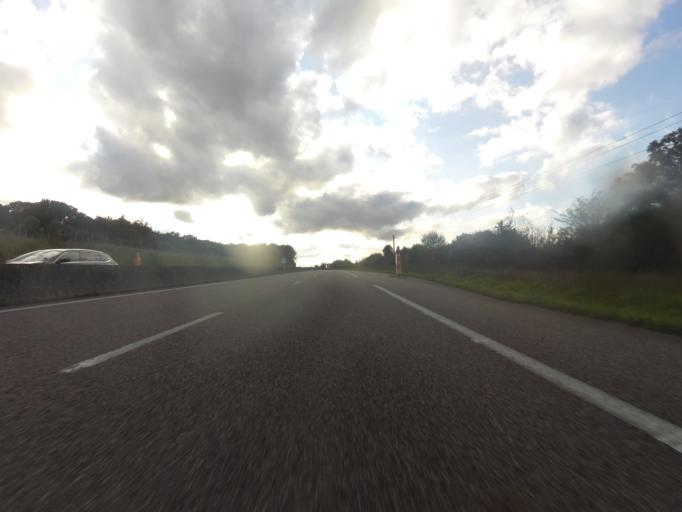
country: FR
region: Haute-Normandie
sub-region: Departement de la Seine-Maritime
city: Aumale
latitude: 49.7783
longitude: 1.7304
